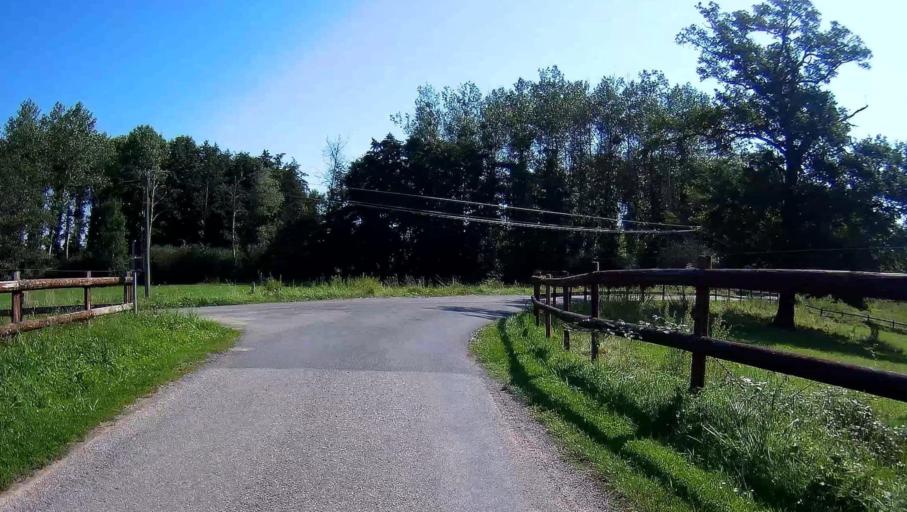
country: FR
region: Bourgogne
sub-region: Departement de Saone-et-Loire
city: Couches
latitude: 46.8381
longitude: 4.5831
